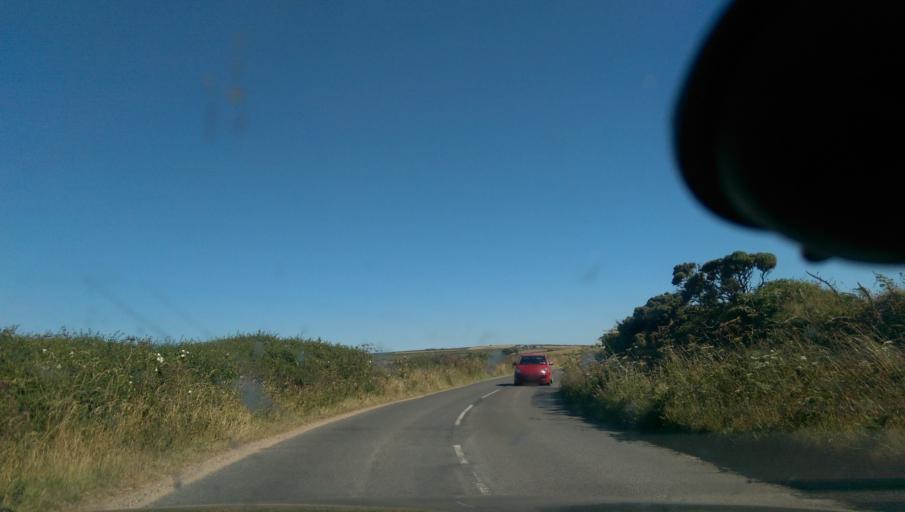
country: GB
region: England
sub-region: Cornwall
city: Sennen
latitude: 50.0653
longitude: -5.6933
